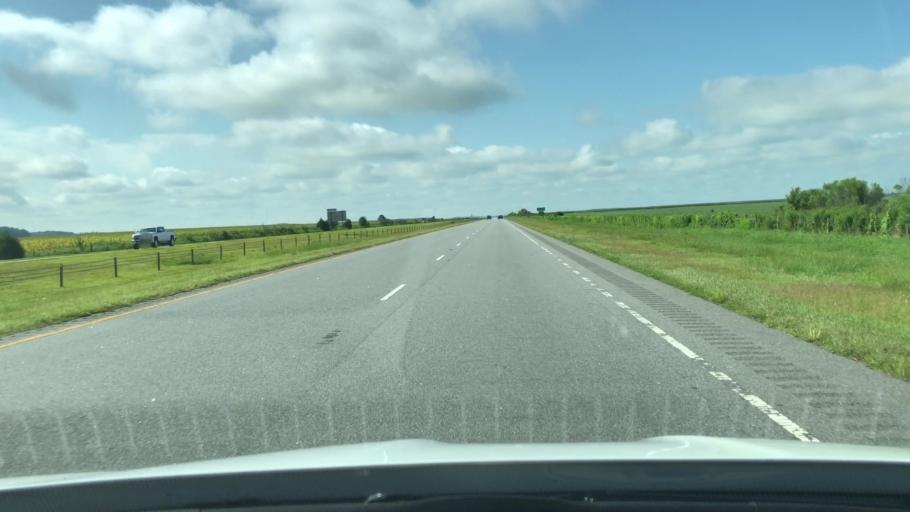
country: US
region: North Carolina
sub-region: Pasquotank County
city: Elizabeth City
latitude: 36.3558
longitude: -76.3151
